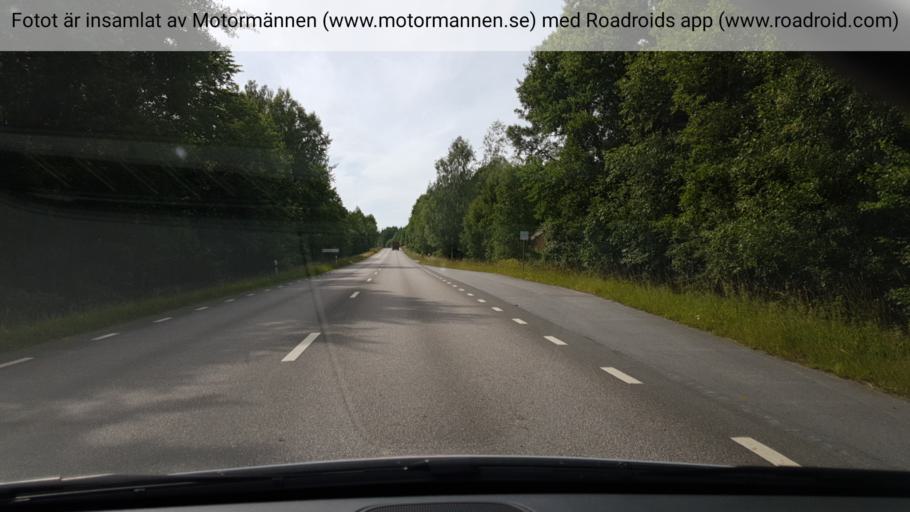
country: SE
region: Vaestra Goetaland
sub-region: Tibro Kommun
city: Tibro
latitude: 58.3417
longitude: 14.1880
